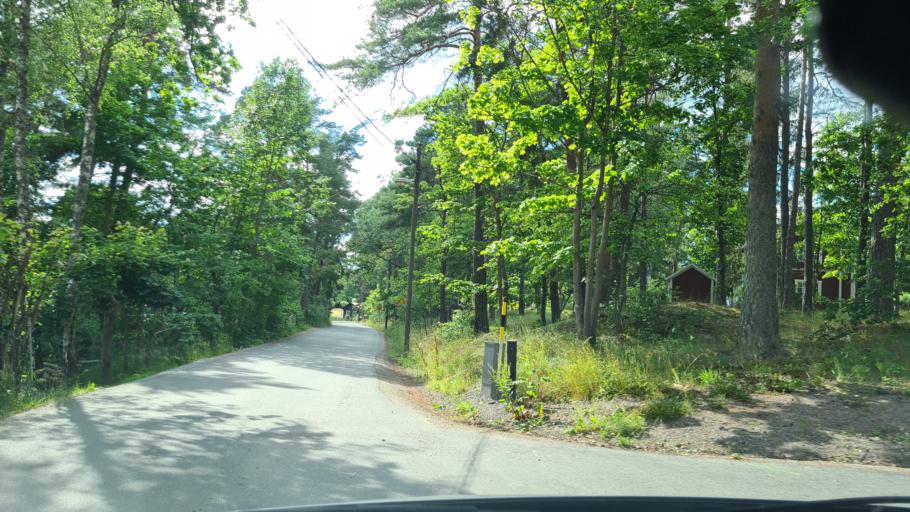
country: SE
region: Stockholm
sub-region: Vaxholms Kommun
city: Vaxholm
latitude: 59.4115
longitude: 18.3748
